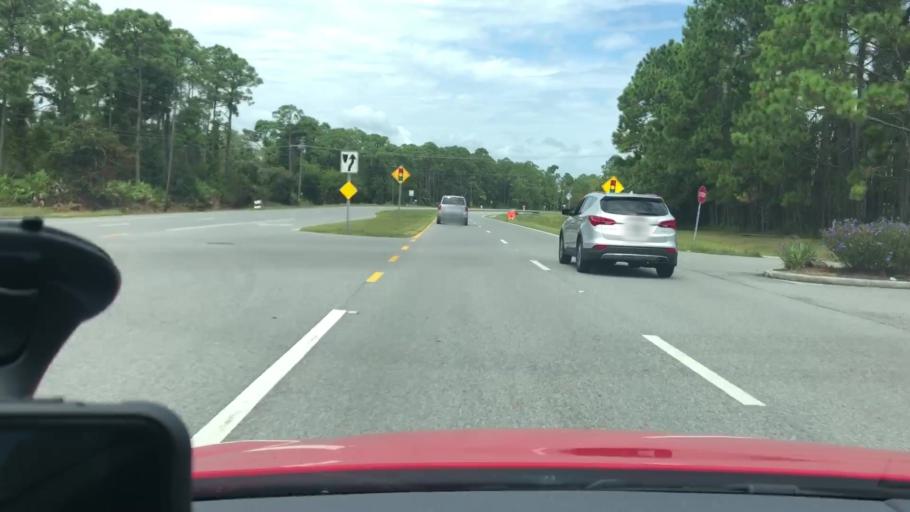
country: US
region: Florida
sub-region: Volusia County
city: Daytona Beach
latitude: 29.2055
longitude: -81.0733
